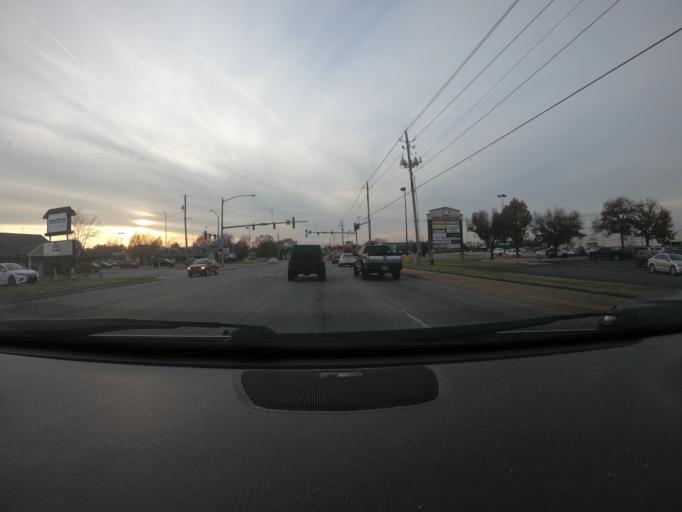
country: US
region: Arkansas
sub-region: Benton County
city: Rogers
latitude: 36.3341
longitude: -94.1468
